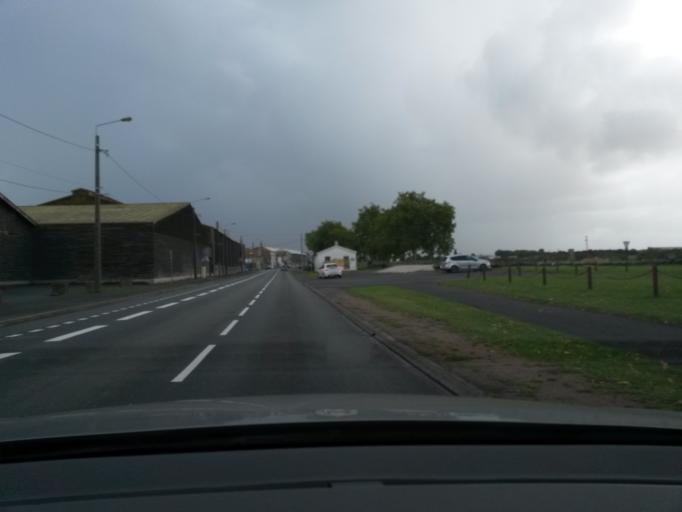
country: FR
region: Poitou-Charentes
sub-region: Departement de la Charente-Maritime
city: Rochefort
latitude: 45.9470
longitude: -0.9532
